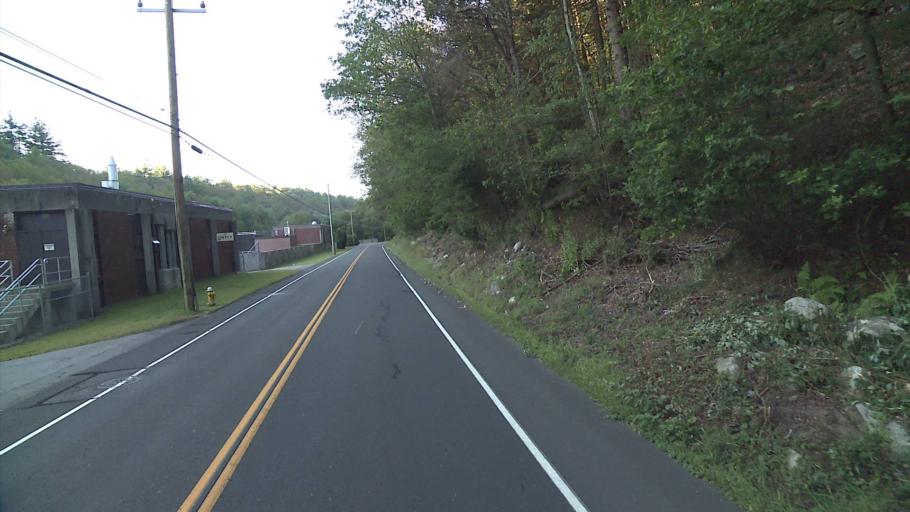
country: US
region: Connecticut
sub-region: Tolland County
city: Stafford Springs
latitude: 41.9477
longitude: -72.3046
